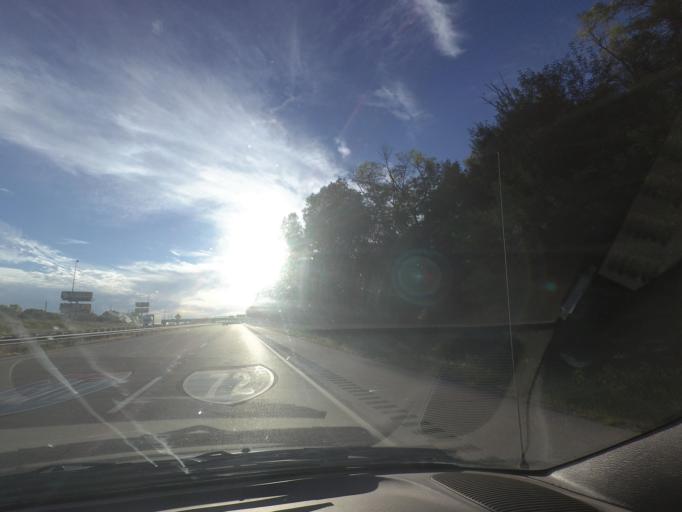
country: US
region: Illinois
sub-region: Sangamon County
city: Southern View
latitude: 39.7453
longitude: -89.6336
